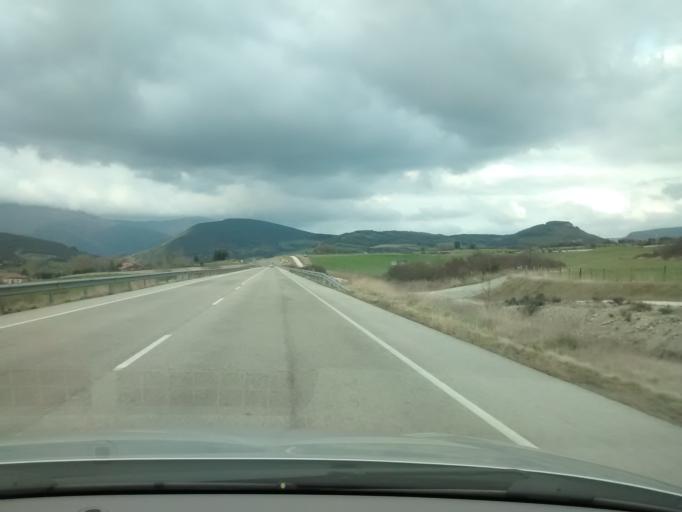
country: ES
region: Castille and Leon
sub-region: Provincia de Burgos
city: Villasana de Mena
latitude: 43.1113
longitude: -3.2621
